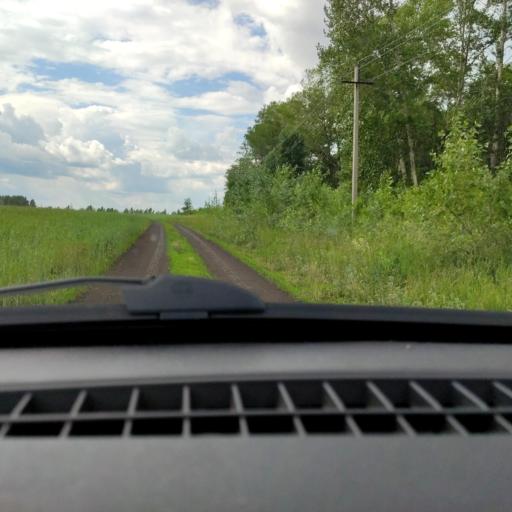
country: RU
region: Bashkortostan
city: Kabakovo
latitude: 54.5232
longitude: 56.0677
